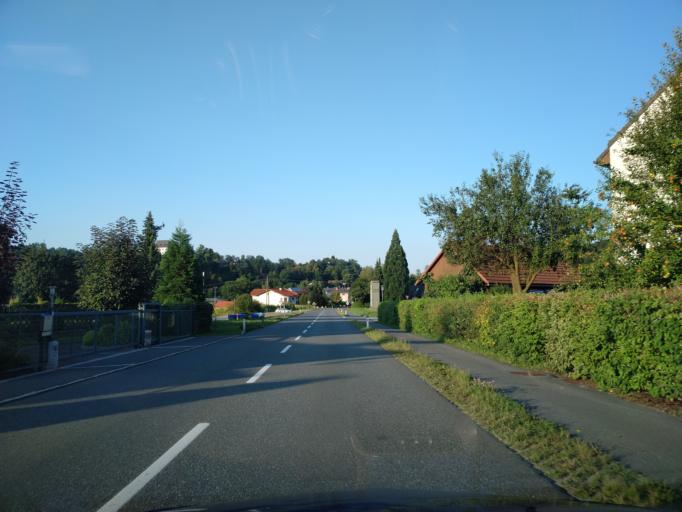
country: AT
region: Styria
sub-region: Politischer Bezirk Deutschlandsberg
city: Wies
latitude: 46.7139
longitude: 15.2607
